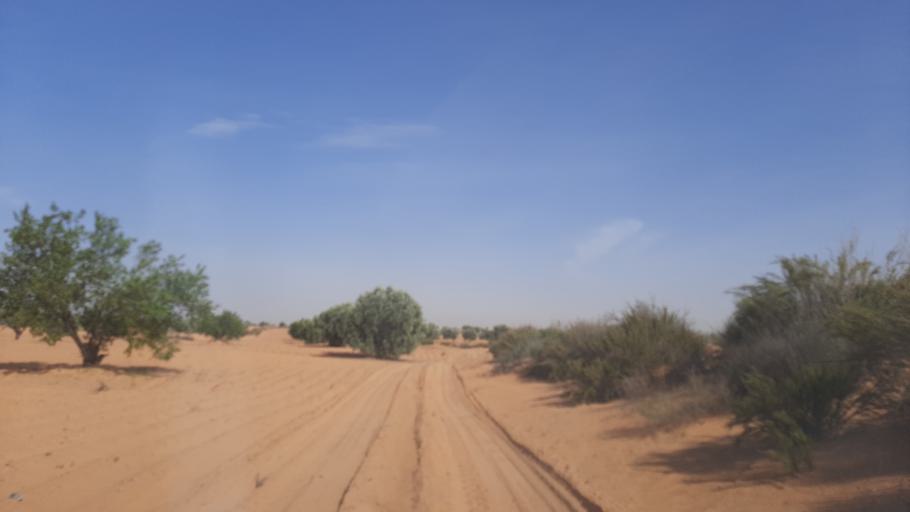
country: TN
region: Madanin
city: Zarzis
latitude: 33.4548
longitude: 10.8107
